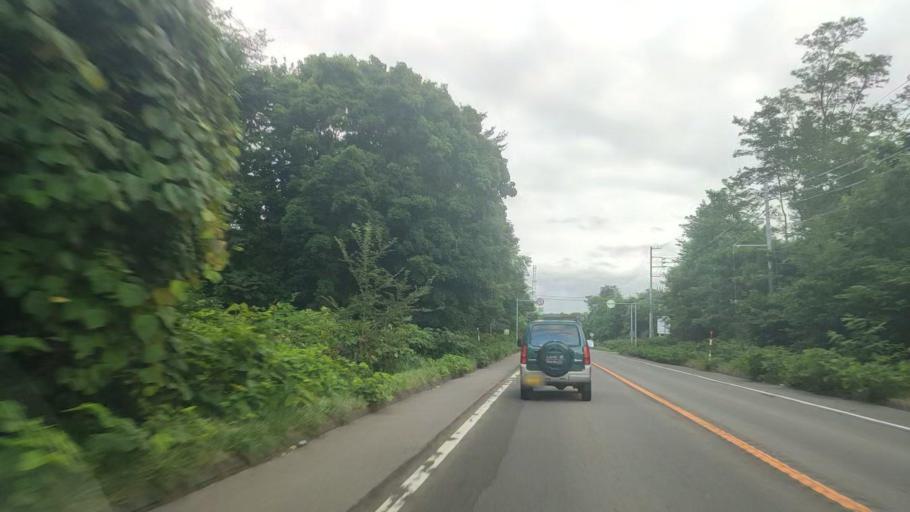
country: JP
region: Hokkaido
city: Nanae
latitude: 42.0698
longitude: 140.6031
